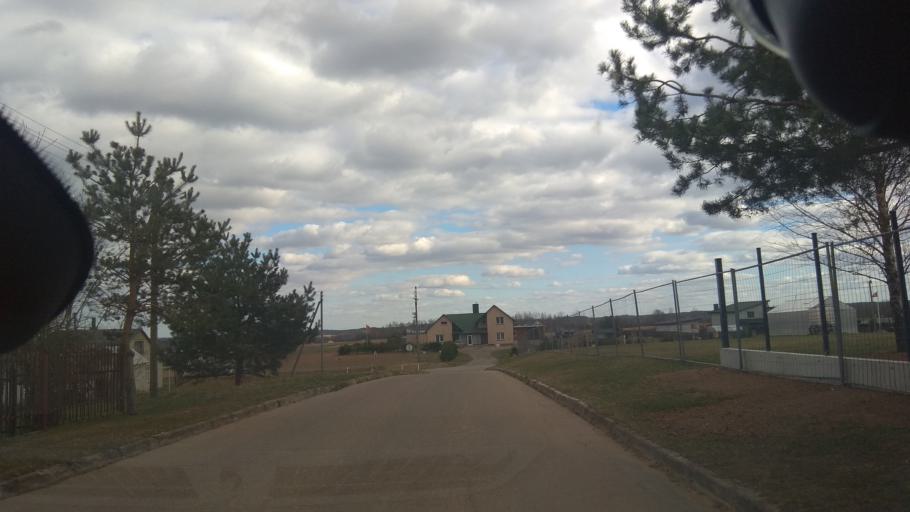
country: LT
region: Vilnius County
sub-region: Vilniaus Rajonas
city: Vievis
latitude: 54.7600
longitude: 24.7993
